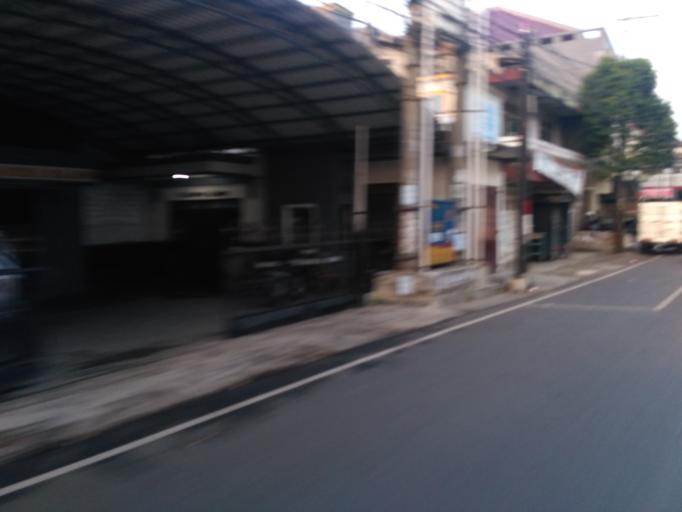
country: ID
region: East Java
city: Malang
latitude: -7.9810
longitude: 112.6283
